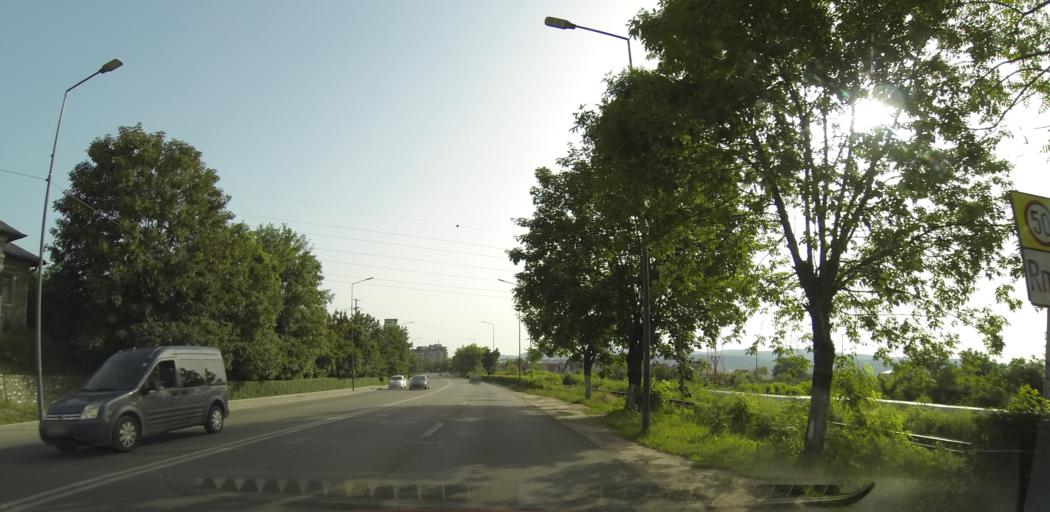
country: RO
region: Valcea
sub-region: Municipiul Ramnicu Valcea
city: Ramnicu Valcea
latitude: 45.0859
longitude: 24.3581
